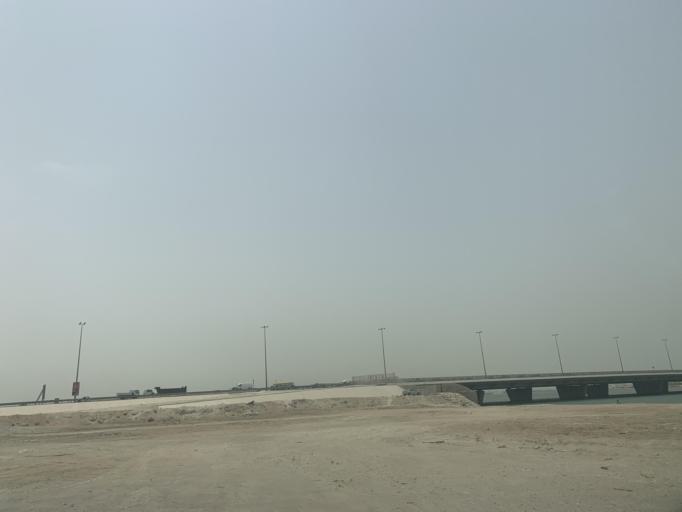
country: BH
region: Northern
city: Sitrah
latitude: 26.1747
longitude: 50.5995
